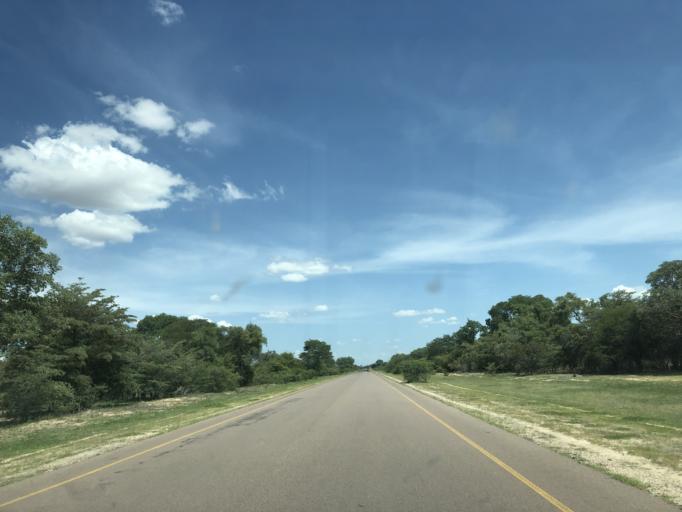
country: AO
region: Cunene
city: Ondjiva
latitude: -16.8701
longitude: 15.4801
